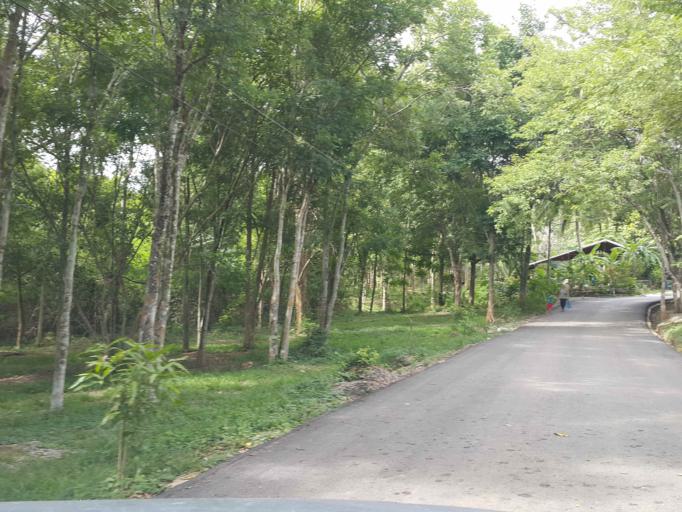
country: TH
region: Sukhothai
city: Thung Saliam
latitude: 17.2438
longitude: 99.4867
